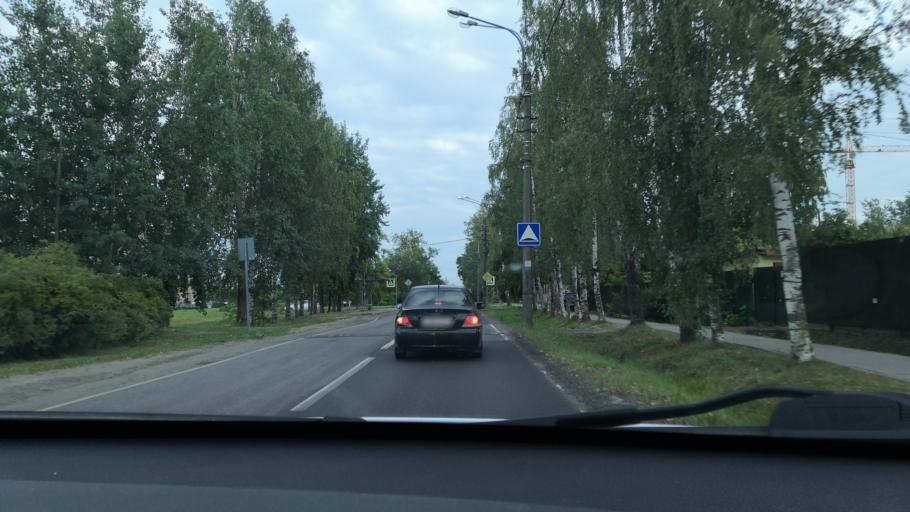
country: RU
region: St.-Petersburg
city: Pushkin
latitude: 59.6974
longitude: 30.4113
